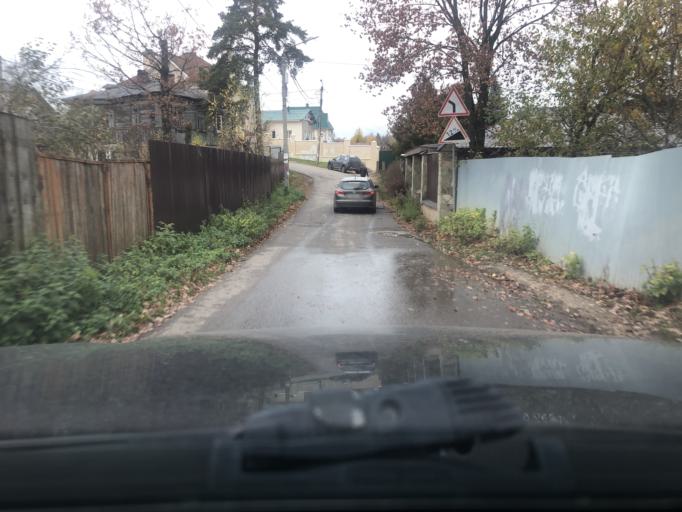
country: RU
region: Moskovskaya
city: Sergiyev Posad
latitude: 56.3117
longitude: 38.1231
